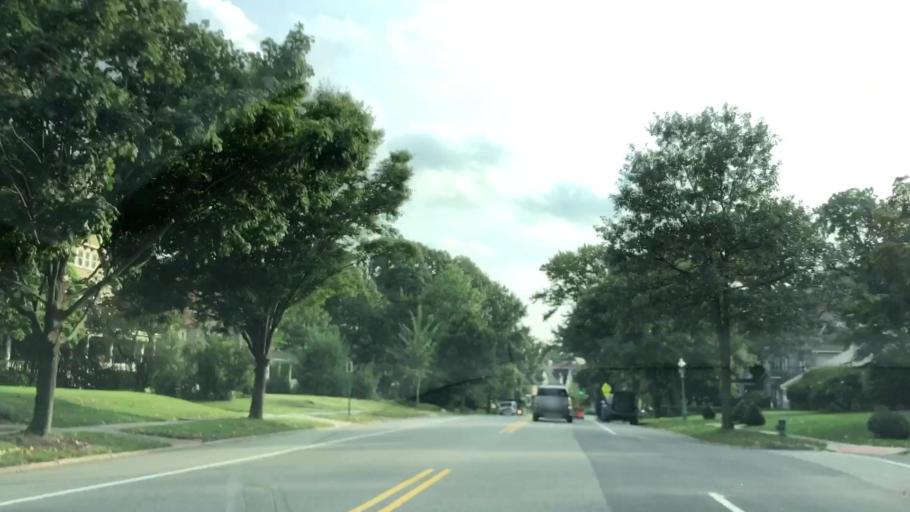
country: US
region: New Jersey
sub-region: Essex County
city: Glen Ridge
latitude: 40.8041
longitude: -74.2016
